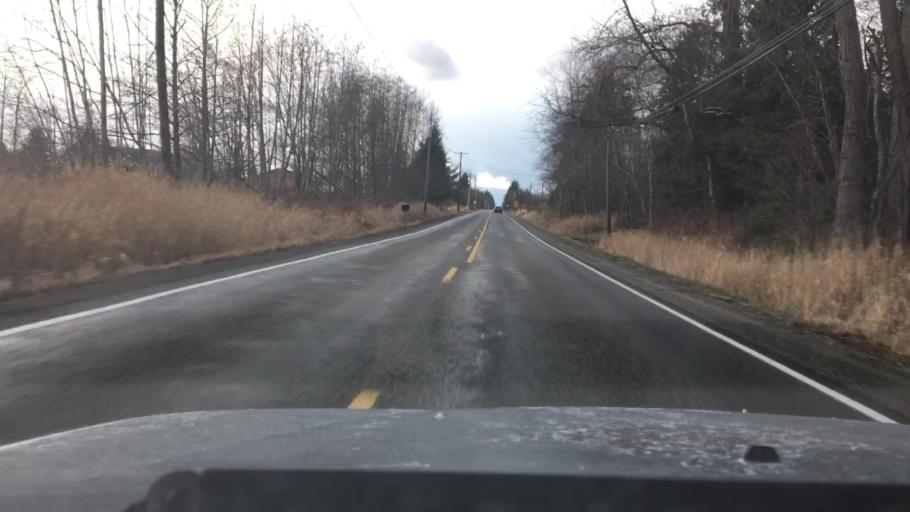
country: US
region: Washington
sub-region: Whatcom County
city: Ferndale
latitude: 48.8483
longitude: -122.6561
